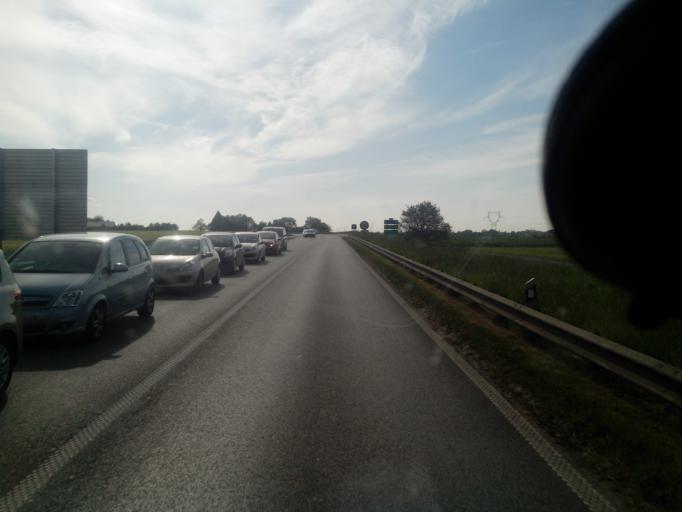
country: FR
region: Nord-Pas-de-Calais
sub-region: Departement du Nord
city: Hazebrouck
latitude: 50.7406
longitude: 2.5461
